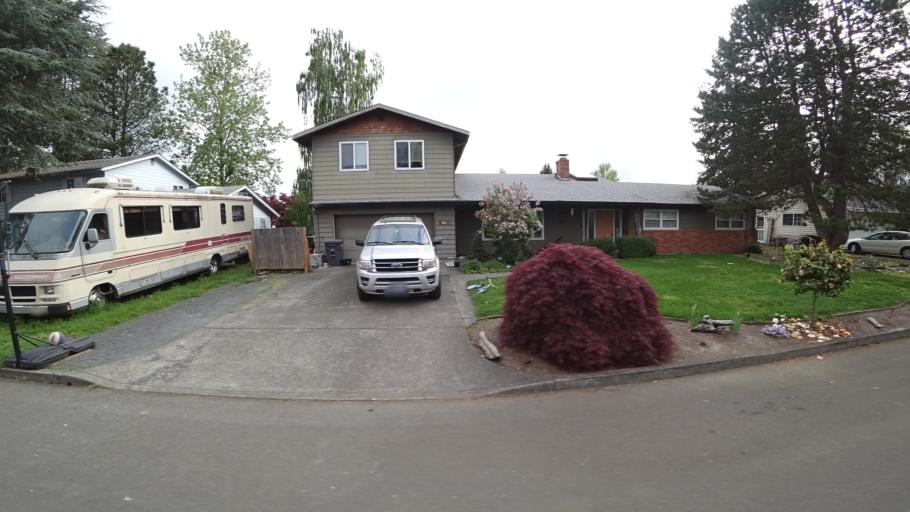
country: US
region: Oregon
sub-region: Washington County
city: Hillsboro
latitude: 45.5301
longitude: -122.9707
